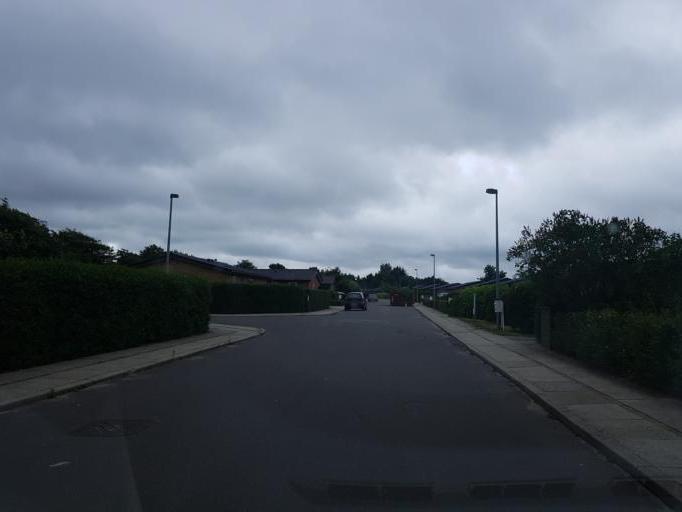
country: DK
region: South Denmark
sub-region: Varde Kommune
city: Varde
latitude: 55.6105
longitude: 8.4691
